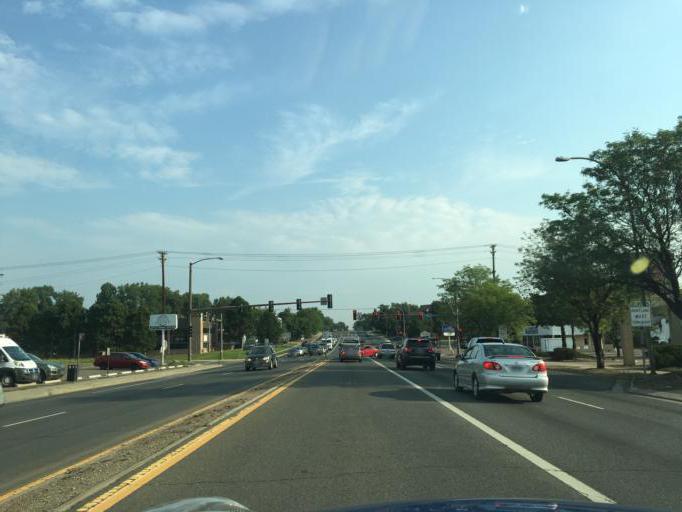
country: US
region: Colorado
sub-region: Jefferson County
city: Edgewater
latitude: 39.7467
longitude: -105.0814
